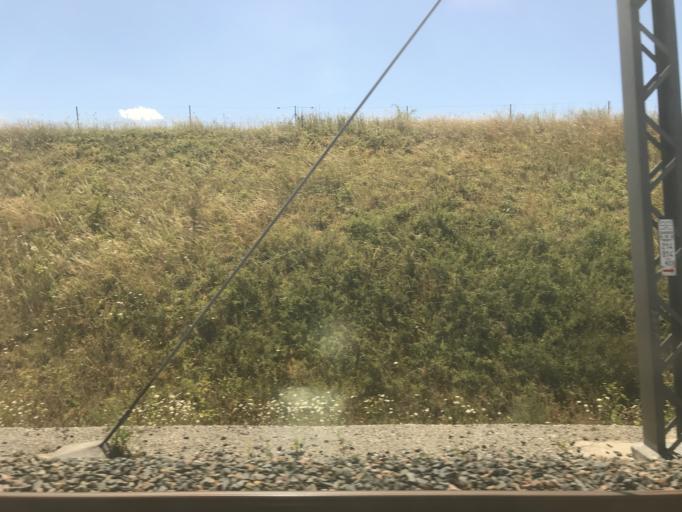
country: FR
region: Lorraine
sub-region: Departement de la Meuse
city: Dugny-sur-Meuse
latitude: 48.9773
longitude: 5.2878
